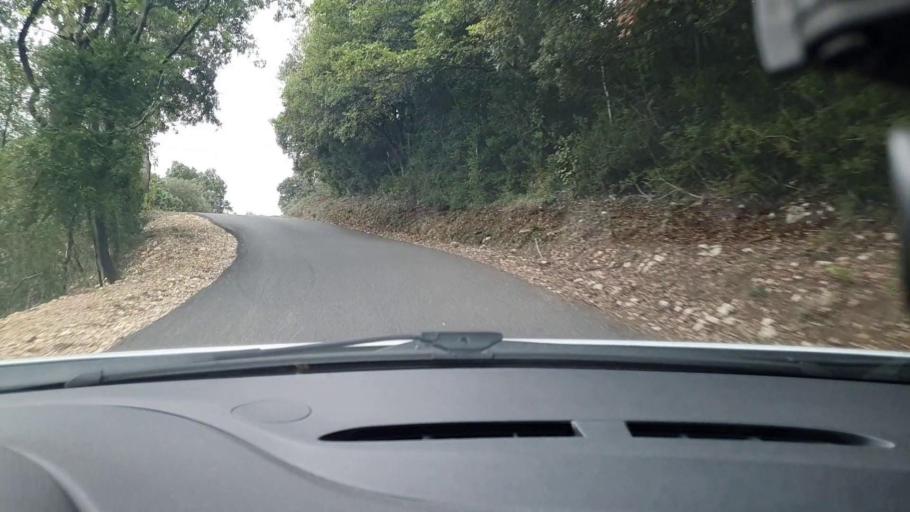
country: FR
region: Languedoc-Roussillon
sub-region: Departement du Gard
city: Mons
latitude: 44.1413
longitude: 4.2900
